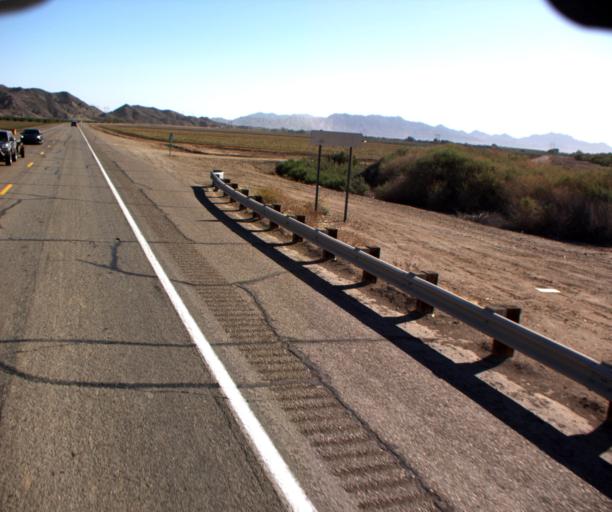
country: US
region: Arizona
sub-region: Yuma County
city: Fortuna Foothills
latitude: 32.7619
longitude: -114.4111
